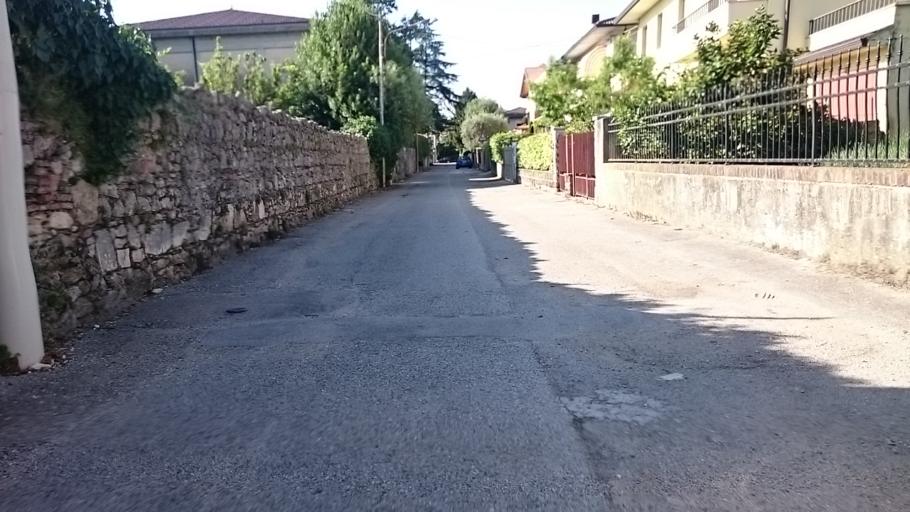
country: IT
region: Veneto
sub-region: Provincia di Vicenza
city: Vicenza
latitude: 45.5280
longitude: 11.5597
